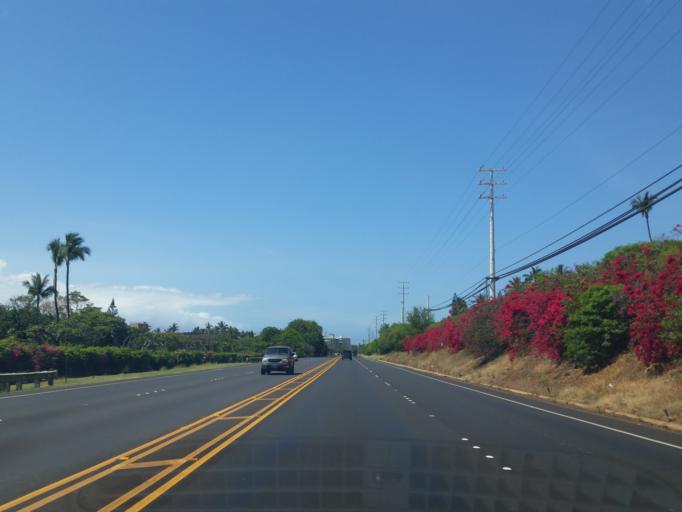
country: US
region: Hawaii
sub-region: Maui County
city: Kaanapali Landing
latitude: 20.9306
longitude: -156.6900
